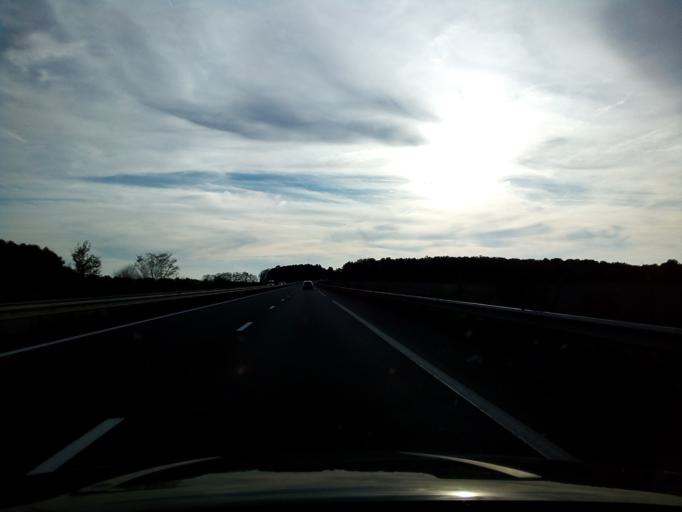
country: FR
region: Poitou-Charentes
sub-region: Departement de la Charente
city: Chasseneuil-sur-Bonnieure
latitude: 45.7982
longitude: 0.4352
